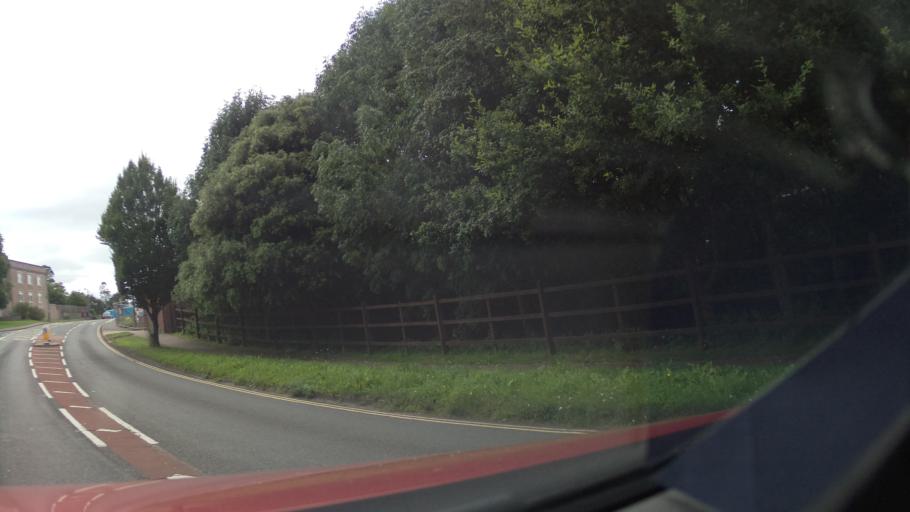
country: GB
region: England
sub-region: Borough of Torbay
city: Torquay
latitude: 50.4832
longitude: -3.5217
